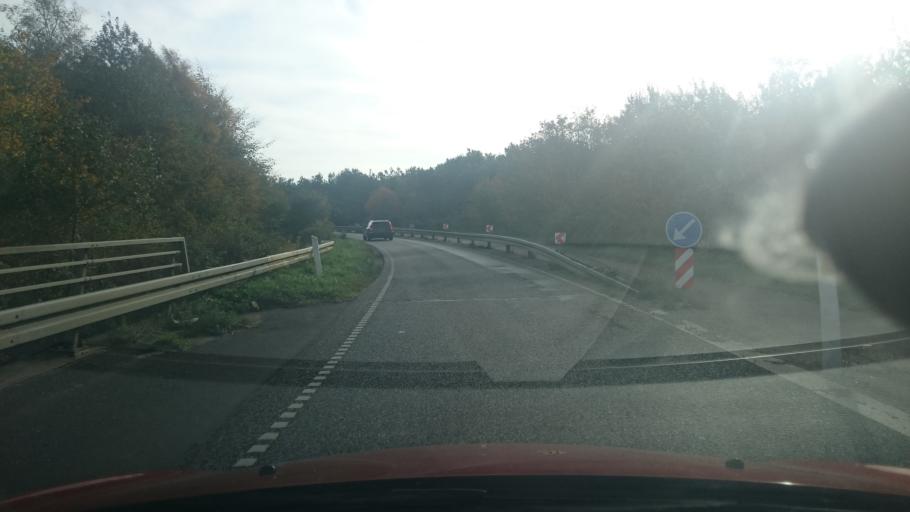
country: DK
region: Central Jutland
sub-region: Randers Kommune
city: Randers
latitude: 56.4421
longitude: 10.0814
